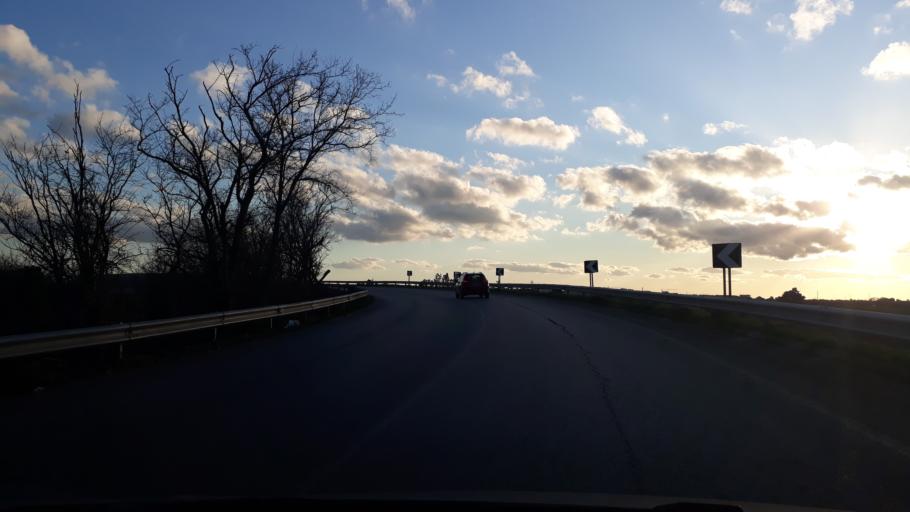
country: IT
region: Apulia
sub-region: Provincia di Brindisi
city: Brindisi
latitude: 40.6537
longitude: 17.9004
